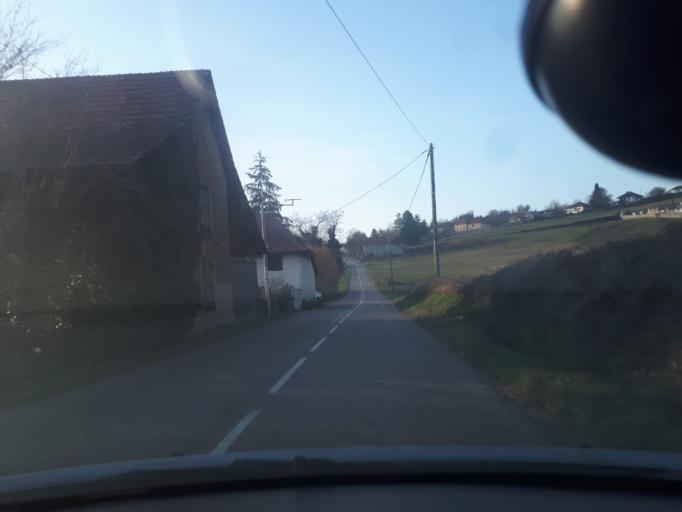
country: FR
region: Rhone-Alpes
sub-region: Departement de l'Isere
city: Sermerieu
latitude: 45.6692
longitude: 5.4166
